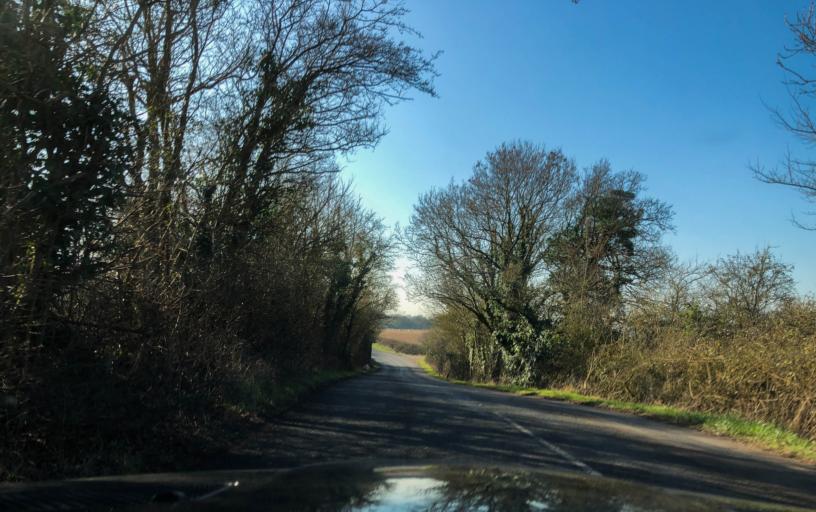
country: GB
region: England
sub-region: Warwickshire
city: Wellesbourne Mountford
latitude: 52.2286
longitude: -1.5626
